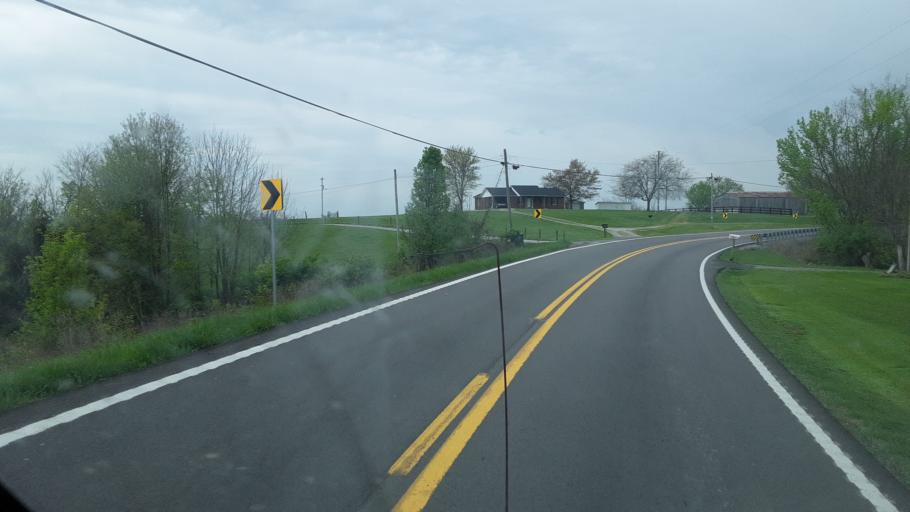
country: US
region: Kentucky
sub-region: Grant County
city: Dry Ridge
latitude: 38.6654
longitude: -84.6414
